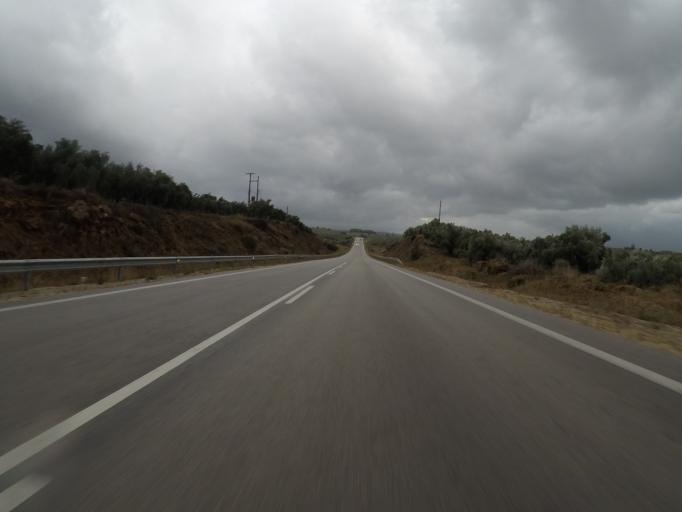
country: GR
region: Peloponnese
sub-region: Nomos Messinias
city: Gargalianoi
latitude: 37.0142
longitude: 21.6486
